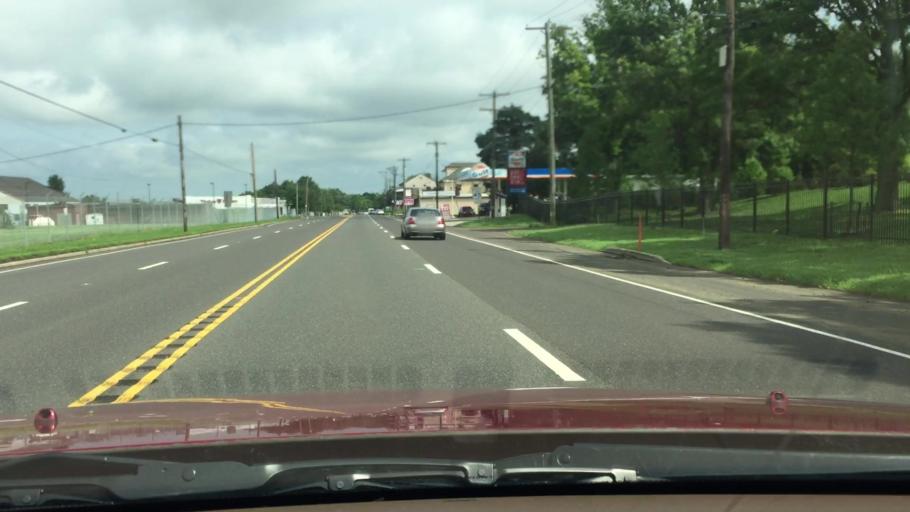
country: US
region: Pennsylvania
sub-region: Montgomery County
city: Horsham
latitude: 40.1944
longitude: -75.1375
